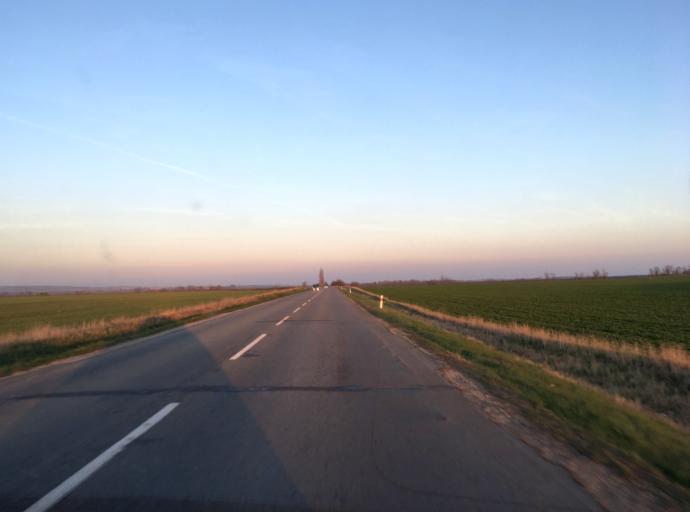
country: SK
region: Nitriansky
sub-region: Okres Komarno
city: Hurbanovo
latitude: 47.9052
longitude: 18.3381
